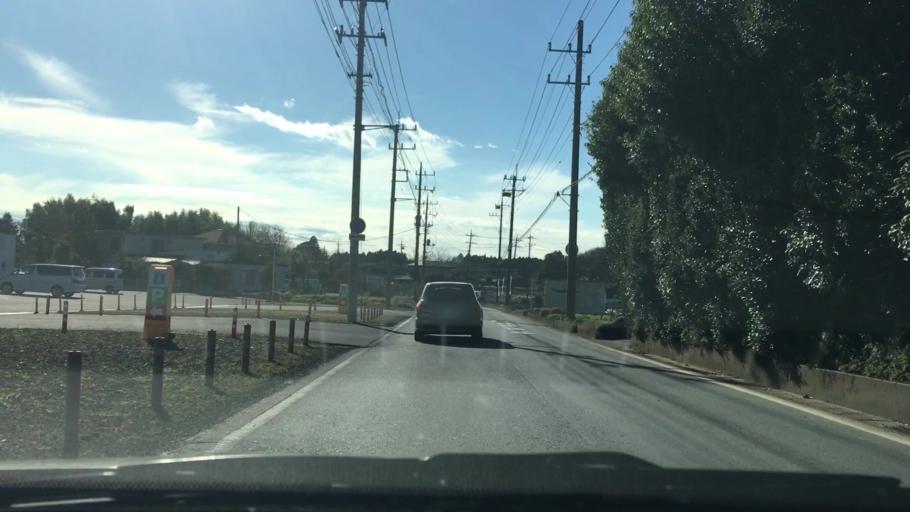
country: JP
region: Chiba
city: Sawara
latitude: 35.8322
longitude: 140.5368
